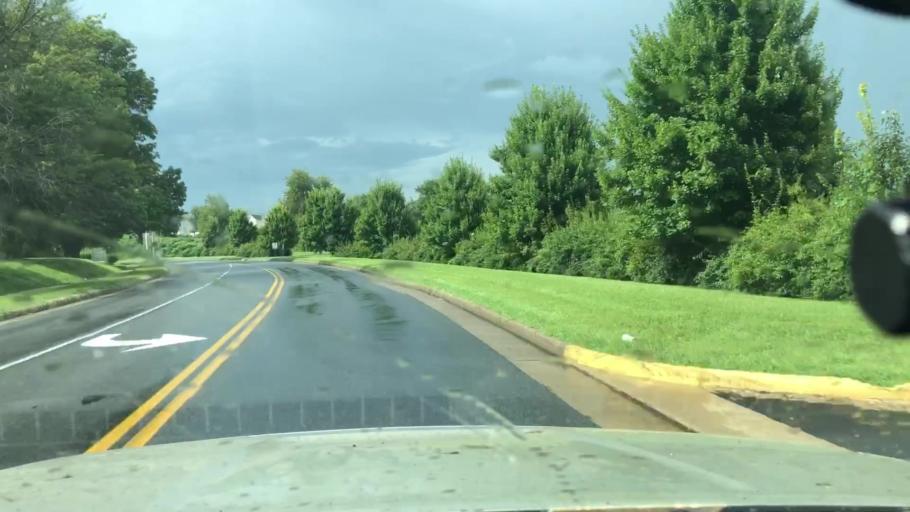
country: US
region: Virginia
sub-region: City of Waynesboro
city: Waynesboro
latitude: 38.0806
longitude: -78.8964
